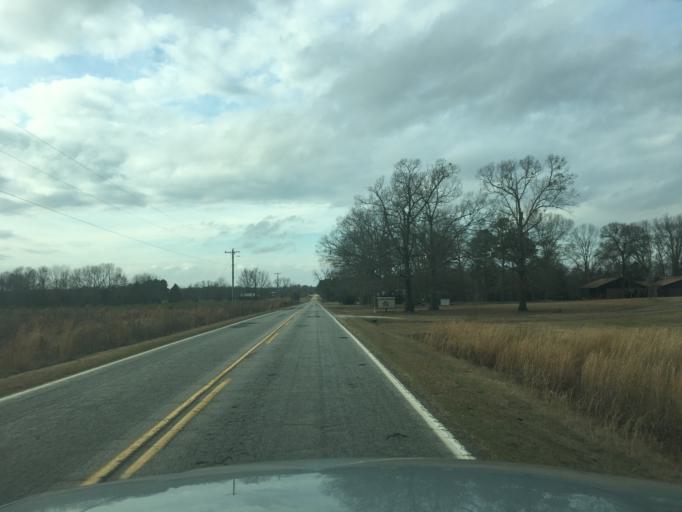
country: US
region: South Carolina
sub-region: Abbeville County
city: Due West
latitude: 34.3284
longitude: -82.4769
